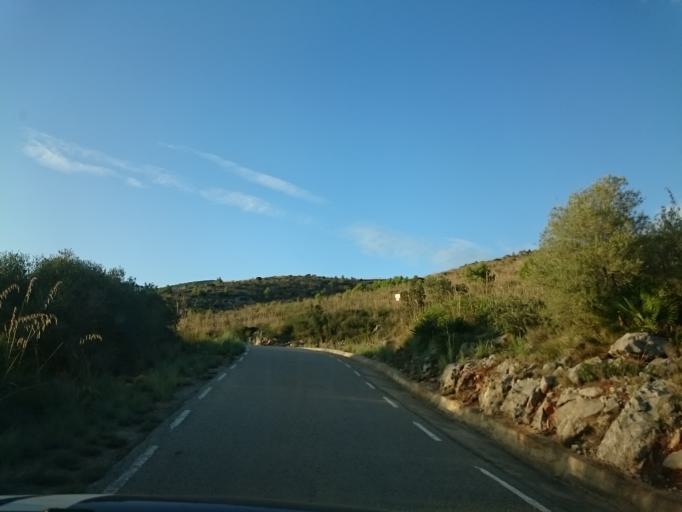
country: ES
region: Catalonia
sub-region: Provincia de Barcelona
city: Olivella
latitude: 41.3002
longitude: 1.8532
